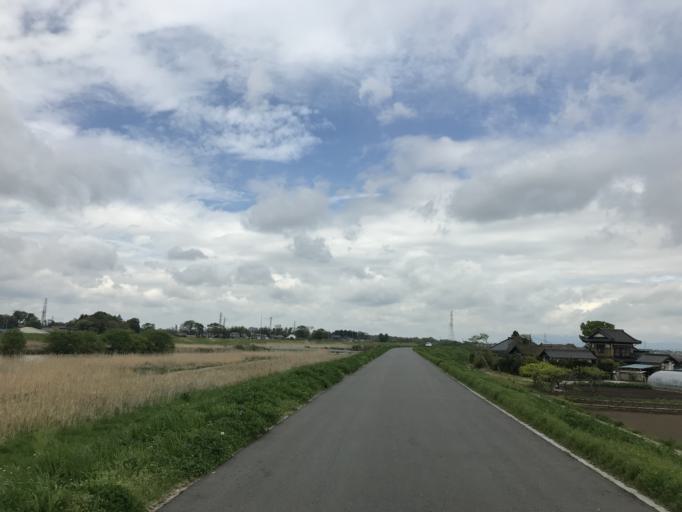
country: JP
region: Ibaraki
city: Mitsukaido
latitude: 35.9994
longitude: 139.9930
